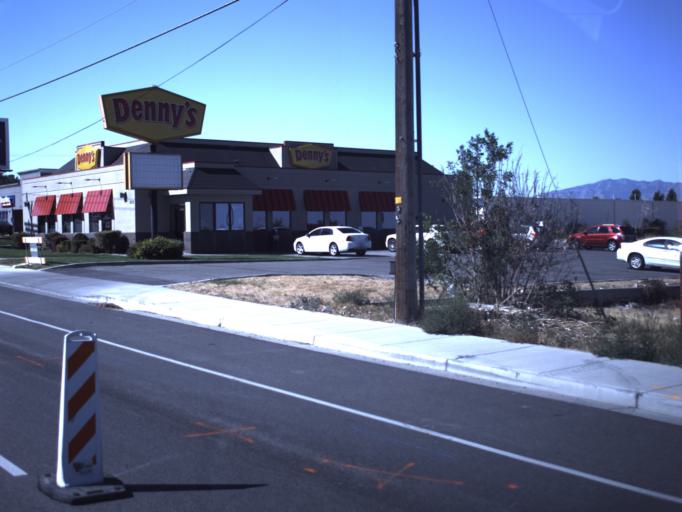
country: US
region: Utah
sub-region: Tooele County
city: Tooele
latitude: 40.5479
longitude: -112.2983
